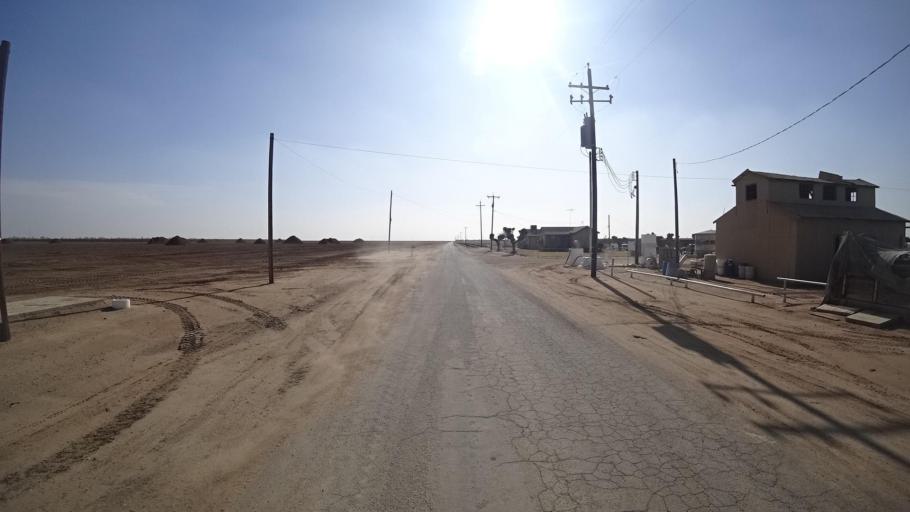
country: US
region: California
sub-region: Kern County
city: Shafter
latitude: 35.5369
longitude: -119.1336
